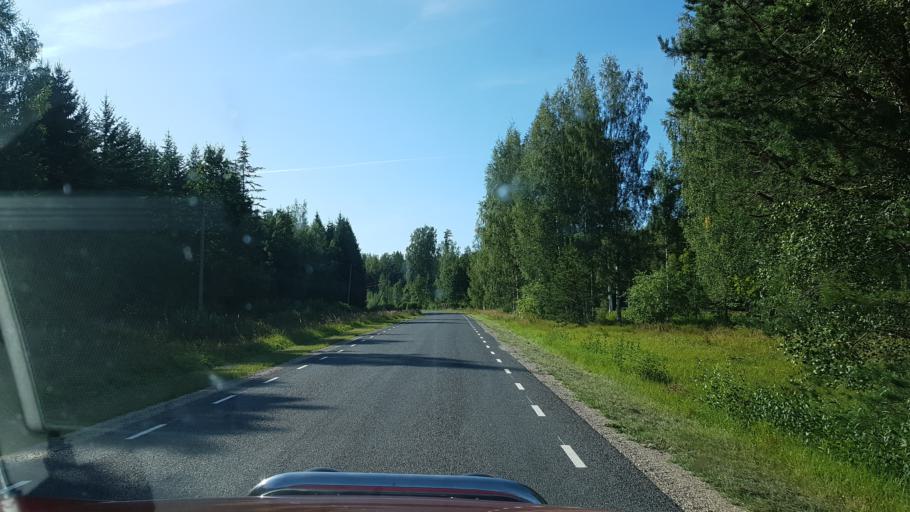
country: LV
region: Aloja
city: Staicele
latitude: 58.0919
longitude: 24.6743
